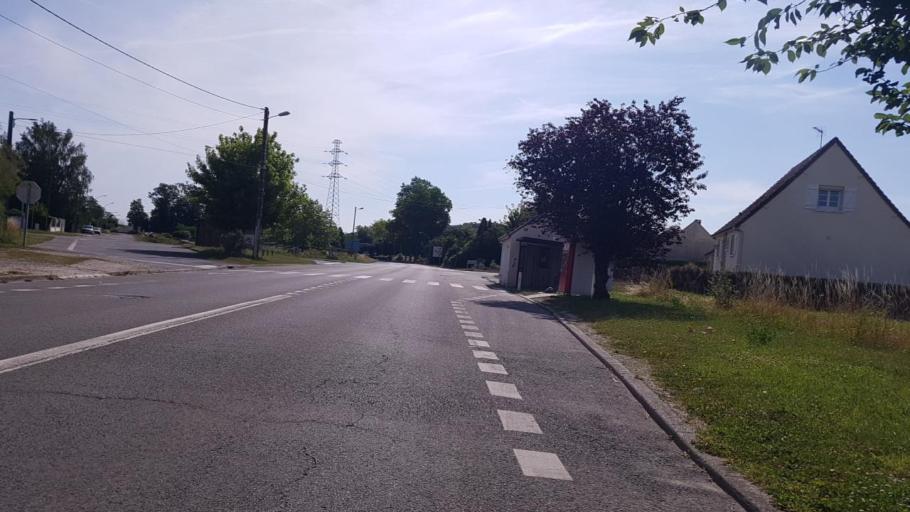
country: FR
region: Picardie
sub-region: Departement de l'Oise
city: Pontpoint
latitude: 49.3077
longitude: 2.6793
